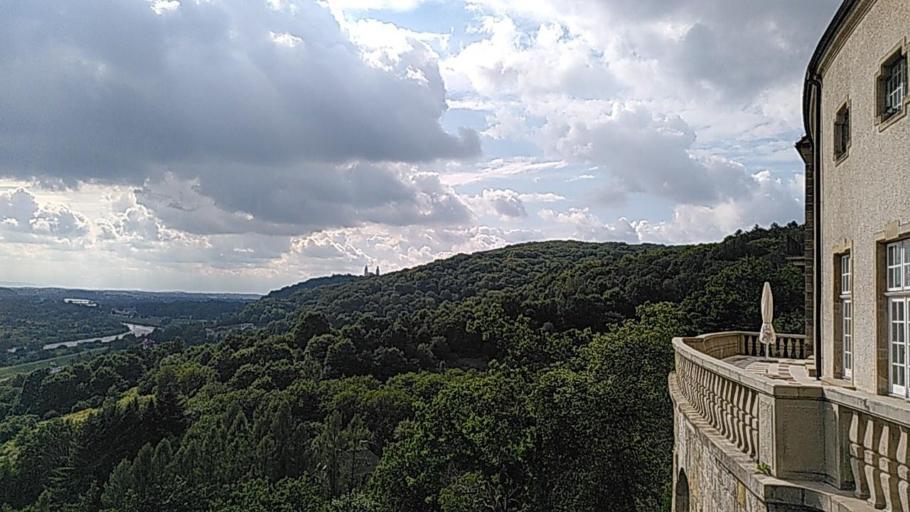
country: PL
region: Lesser Poland Voivodeship
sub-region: Powiat krakowski
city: Rzaska
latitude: 50.0481
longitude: 19.8665
